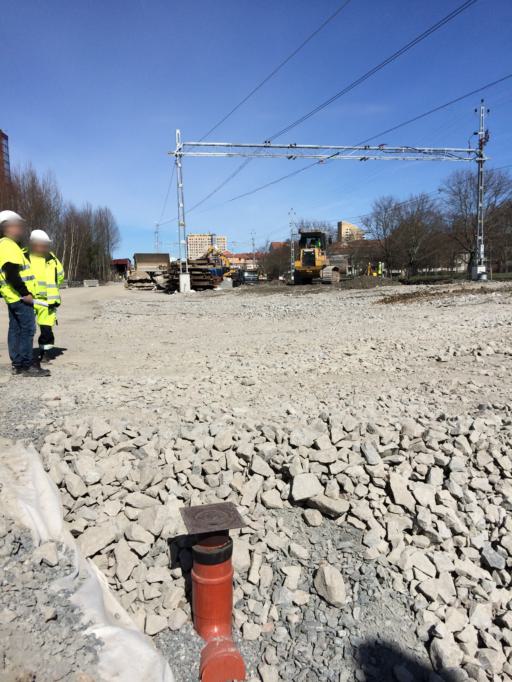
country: SE
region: Stockholm
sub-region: Jarfalla Kommun
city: Jakobsberg
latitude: 59.4186
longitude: 17.8320
